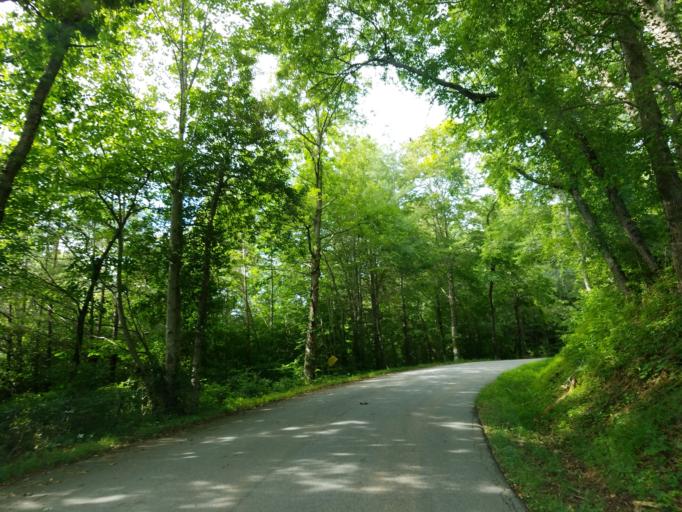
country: US
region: Georgia
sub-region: Union County
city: Blairsville
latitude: 34.7201
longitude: -84.0595
